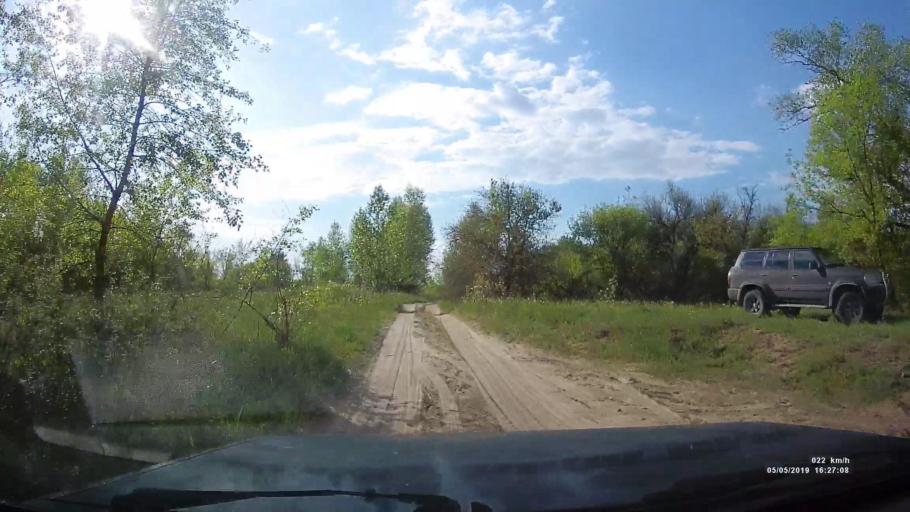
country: RU
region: Rostov
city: Ust'-Donetskiy
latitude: 47.7645
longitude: 41.0198
